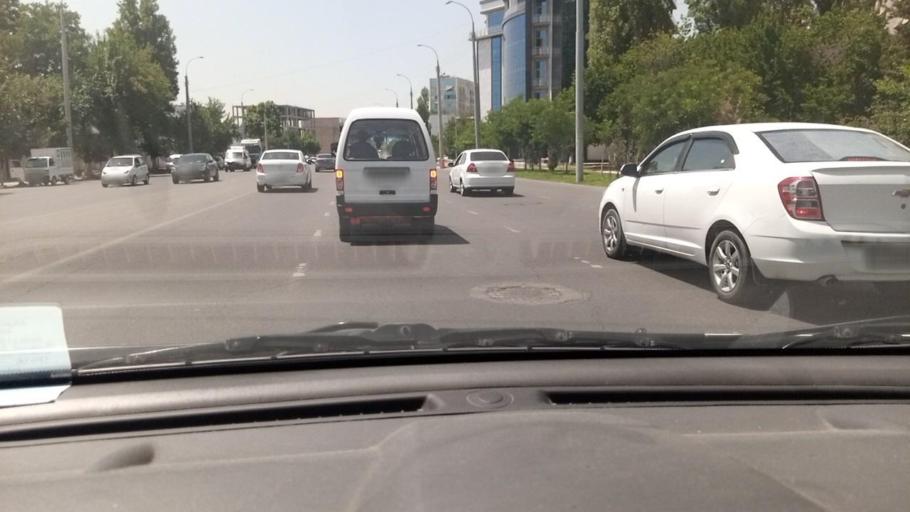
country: UZ
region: Toshkent Shahri
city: Tashkent
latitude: 41.2678
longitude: 69.2512
